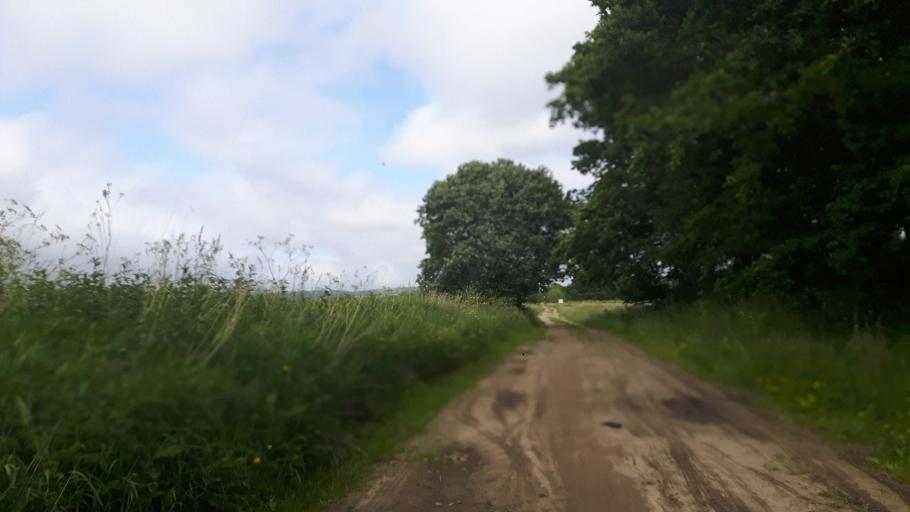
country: PL
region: Pomeranian Voivodeship
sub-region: Powiat slupski
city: Ustka
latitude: 54.5916
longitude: 16.9679
